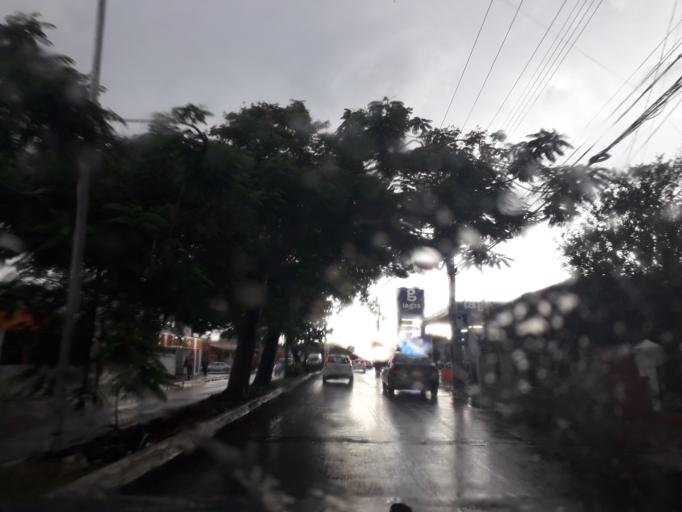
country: MX
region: Yucatan
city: Merida
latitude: 20.9767
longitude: -89.6428
